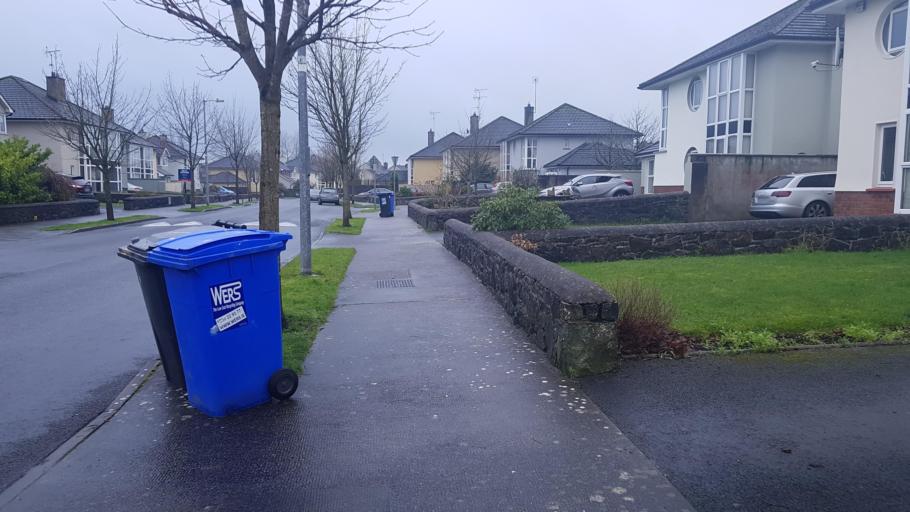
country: IE
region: Connaught
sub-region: County Galway
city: Tuam
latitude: 53.5238
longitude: -8.8477
